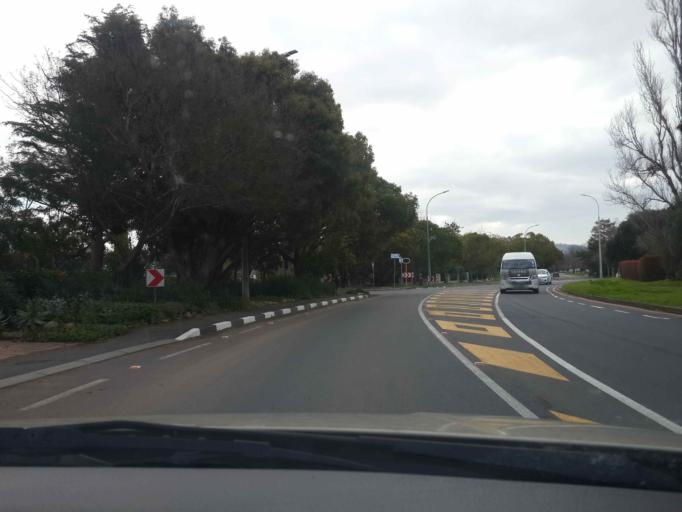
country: ZA
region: Western Cape
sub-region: Cape Winelands District Municipality
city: Stellenbosch
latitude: -33.9359
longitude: 18.8907
